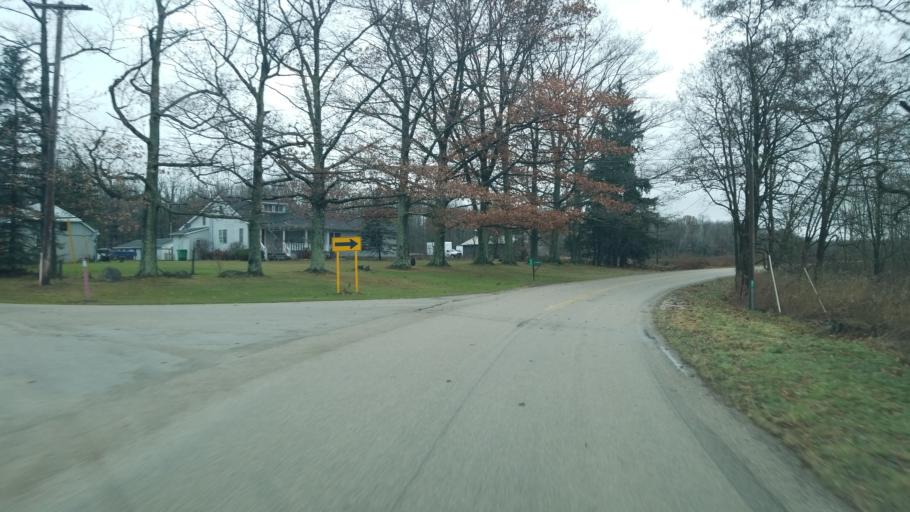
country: US
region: Ohio
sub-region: Ashtabula County
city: Andover
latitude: 41.7247
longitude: -80.6273
